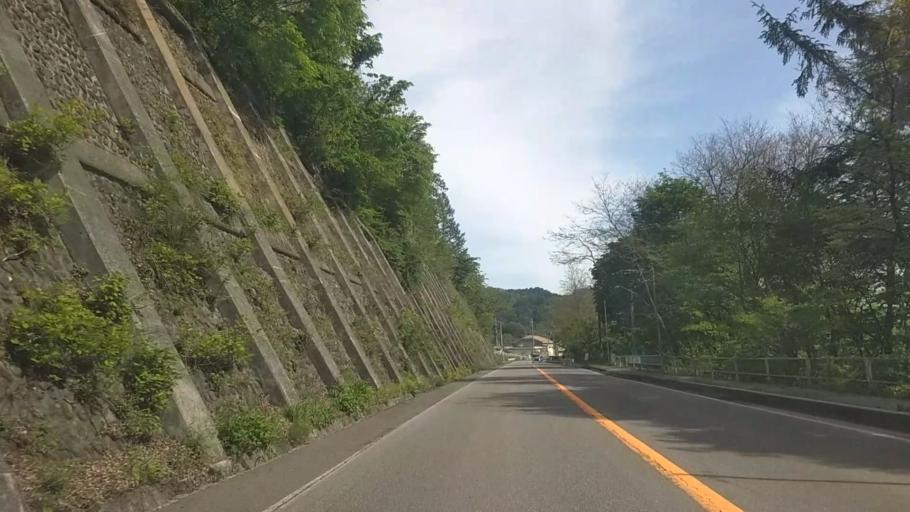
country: JP
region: Nagano
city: Saku
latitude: 36.0537
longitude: 138.4675
